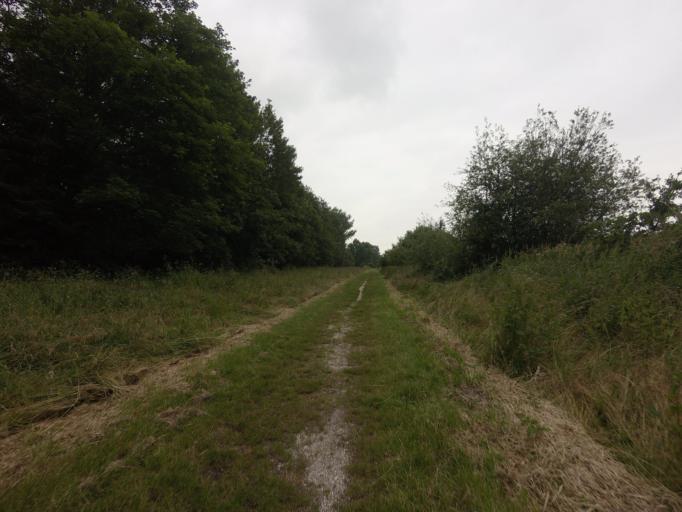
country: NL
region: North Holland
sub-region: Gemeente Huizen
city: Huizen
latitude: 52.3377
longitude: 5.2924
